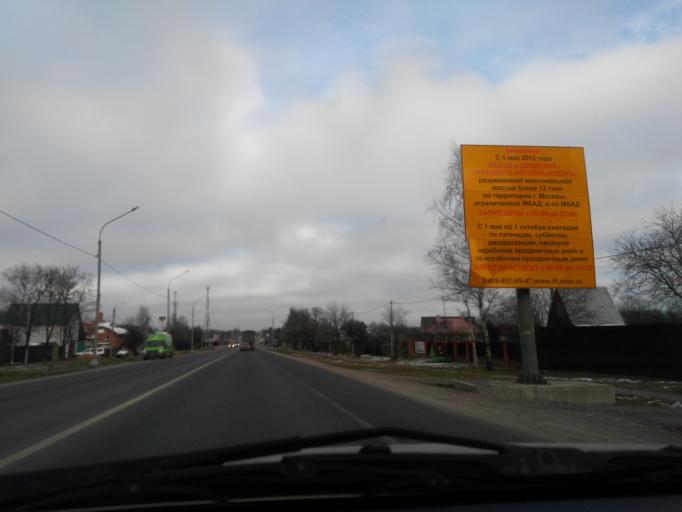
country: RU
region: Moskovskaya
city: Troitsk
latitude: 55.3914
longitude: 37.2298
